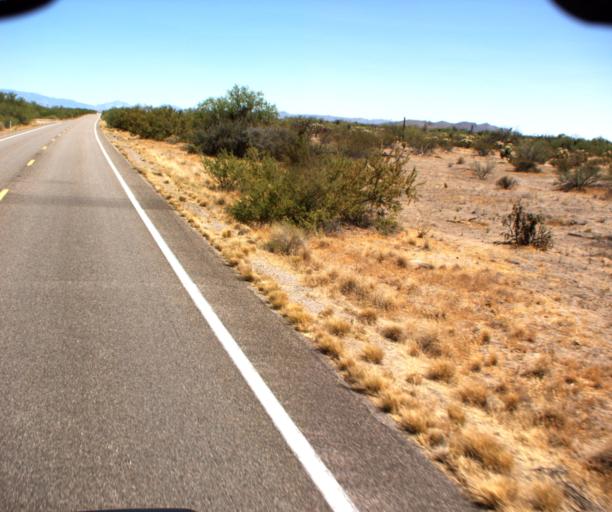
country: US
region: Arizona
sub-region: Pima County
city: Catalina
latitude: 32.7468
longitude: -111.1293
